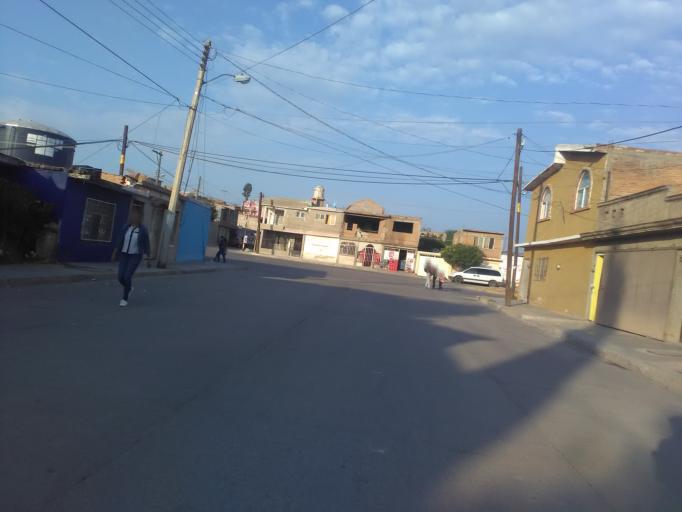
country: MX
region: Durango
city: Victoria de Durango
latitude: 24.0489
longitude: -104.6479
